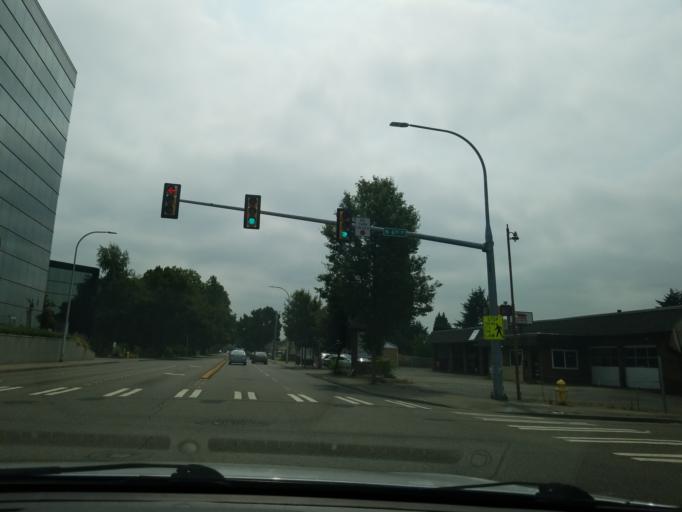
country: US
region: Washington
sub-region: King County
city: Renton
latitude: 47.4922
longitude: -122.2022
